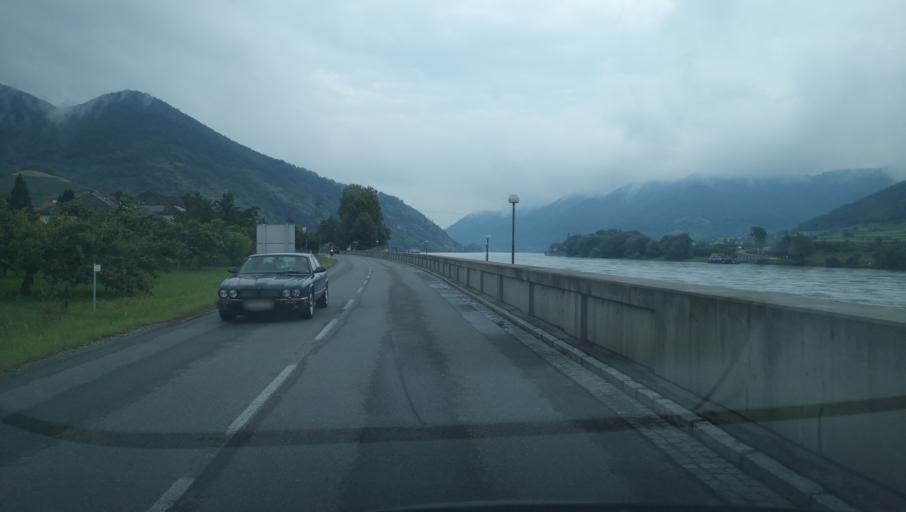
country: AT
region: Lower Austria
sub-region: Politischer Bezirk Krems
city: Spitz
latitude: 48.3597
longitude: 15.4134
